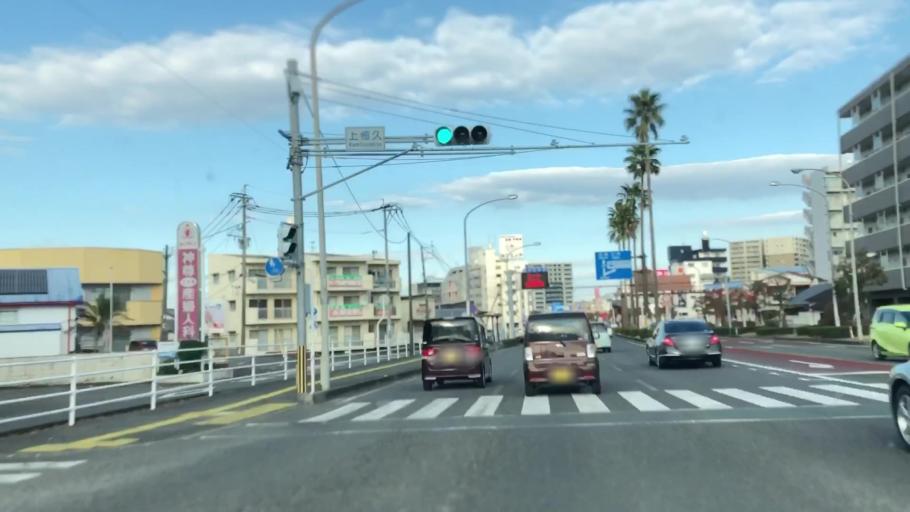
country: JP
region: Miyazaki
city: Miyazaki-shi
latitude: 31.8906
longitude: 131.4136
